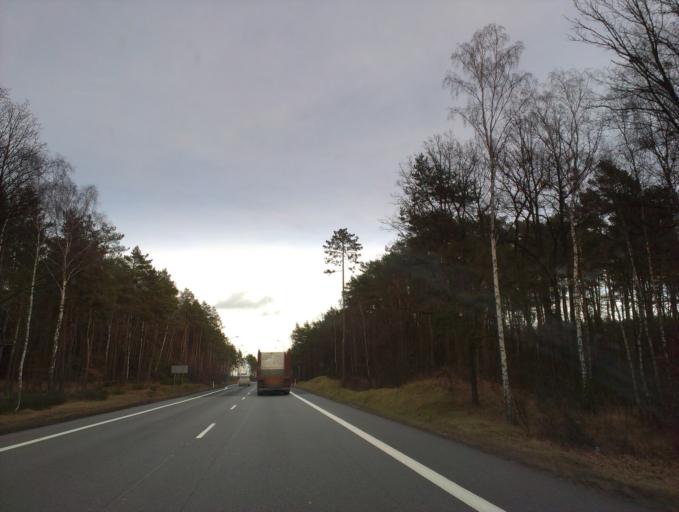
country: PL
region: Kujawsko-Pomorskie
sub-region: Powiat lipnowski
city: Skepe
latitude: 52.8856
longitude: 19.3943
